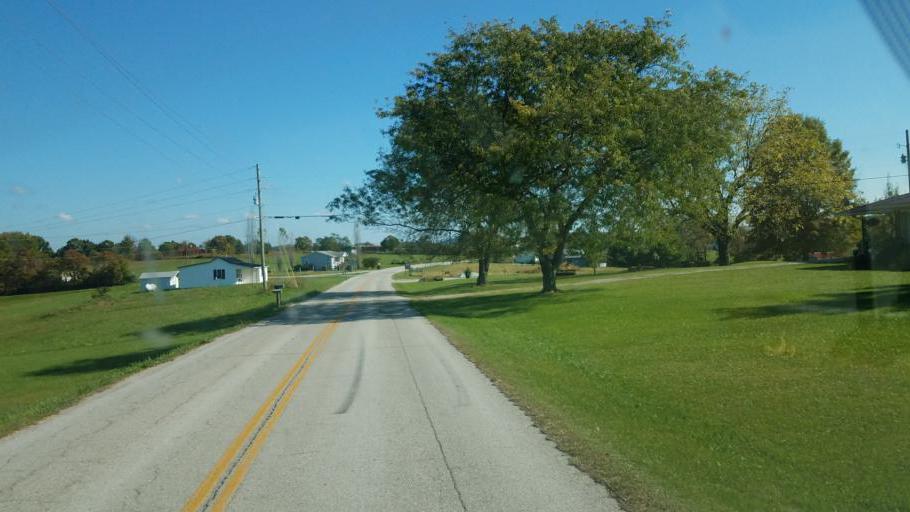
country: US
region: Kentucky
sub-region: Fleming County
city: Flemingsburg
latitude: 38.4611
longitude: -83.5258
